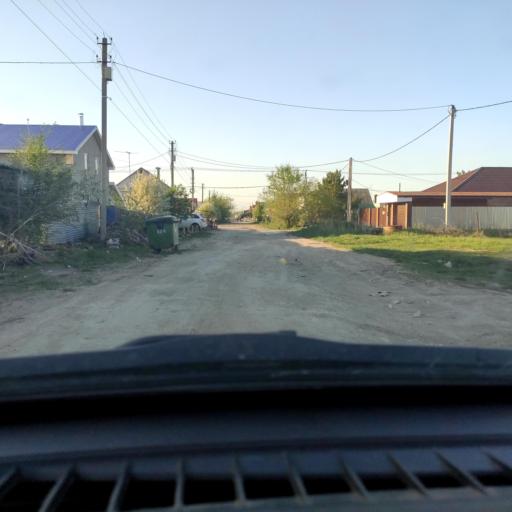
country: RU
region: Samara
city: Tol'yatti
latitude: 53.5623
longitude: 49.4085
